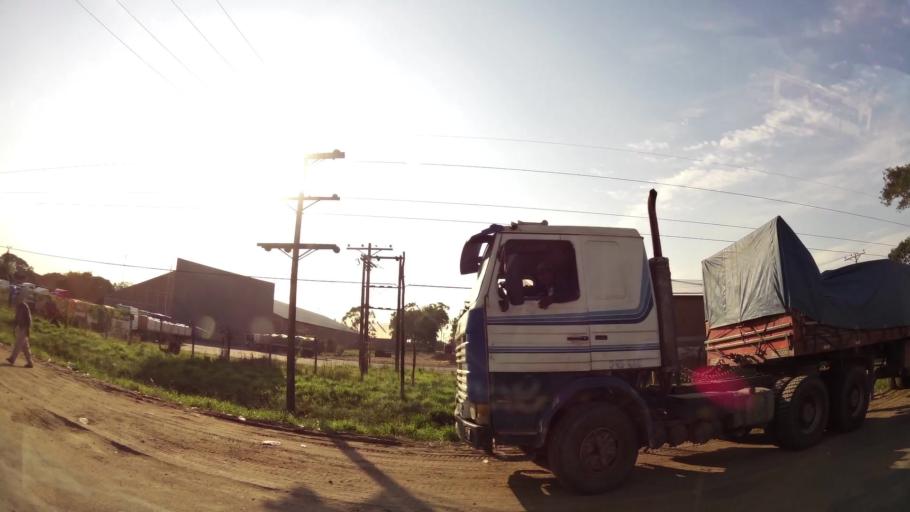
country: BO
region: Santa Cruz
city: Santa Cruz de la Sierra
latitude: -17.6895
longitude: -63.1592
